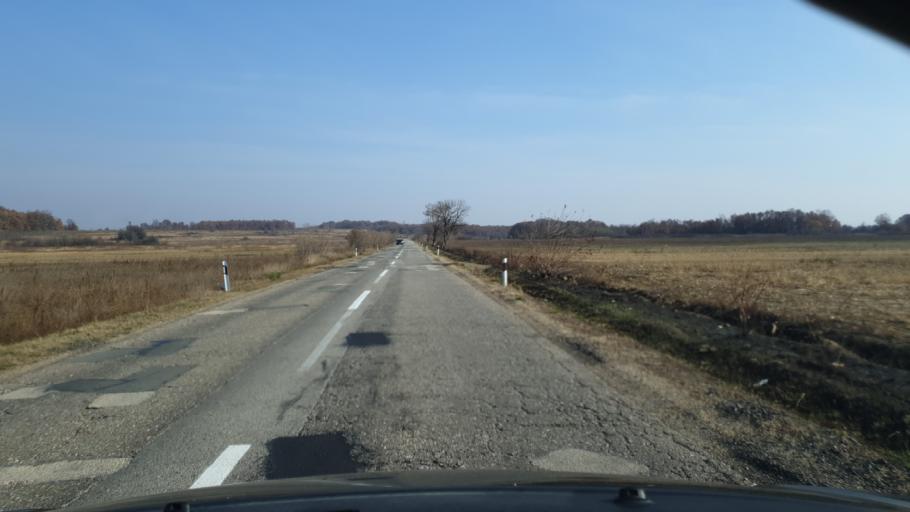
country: RS
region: Central Serbia
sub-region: Borski Okrug
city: Negotin
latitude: 44.2062
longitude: 22.4022
